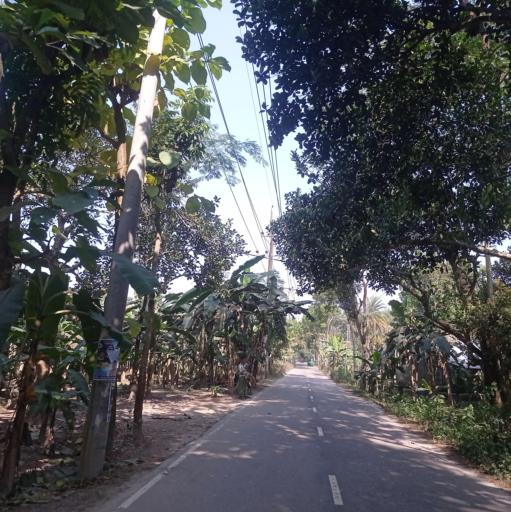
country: BD
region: Dhaka
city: Narsingdi
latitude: 24.0295
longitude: 90.6726
